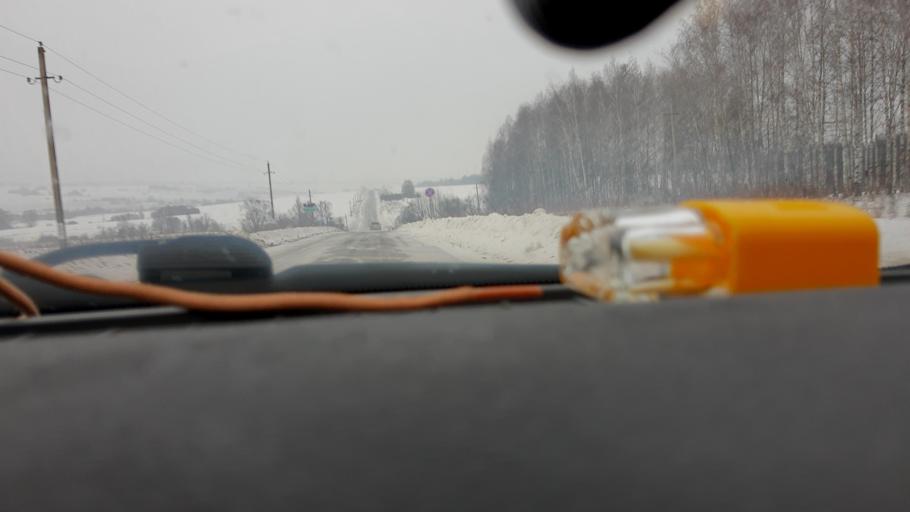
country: RU
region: Bashkortostan
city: Ulukulevo
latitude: 54.5489
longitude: 56.4346
